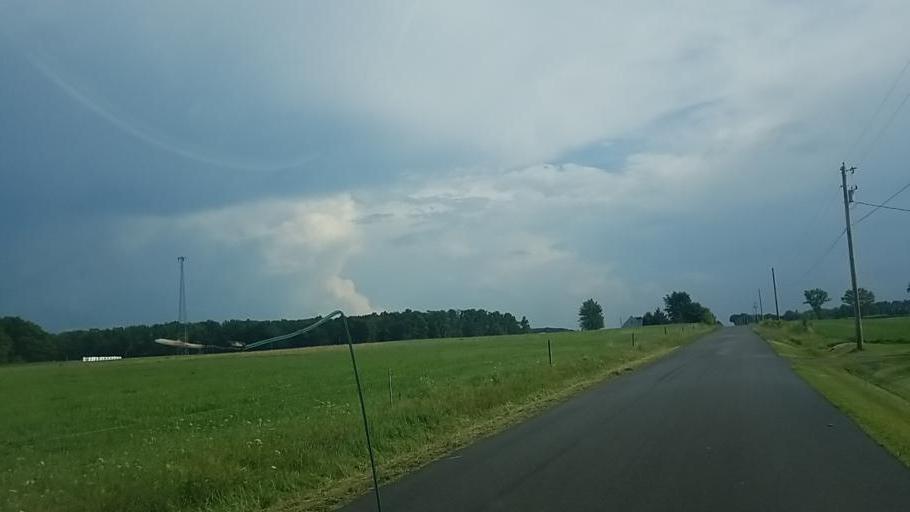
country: US
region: Ohio
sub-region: Wayne County
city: Creston
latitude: 40.9197
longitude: -81.9365
